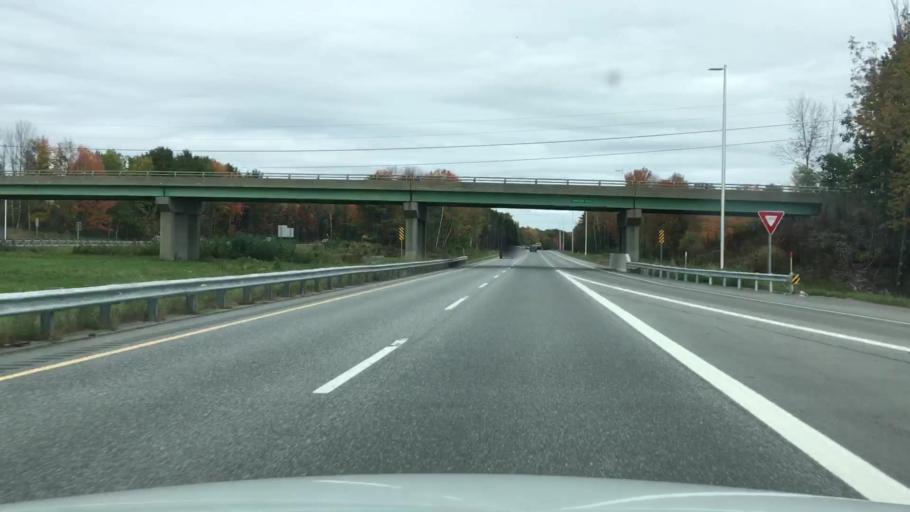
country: US
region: Maine
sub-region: Kennebec County
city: Oakland
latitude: 44.5077
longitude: -69.7029
